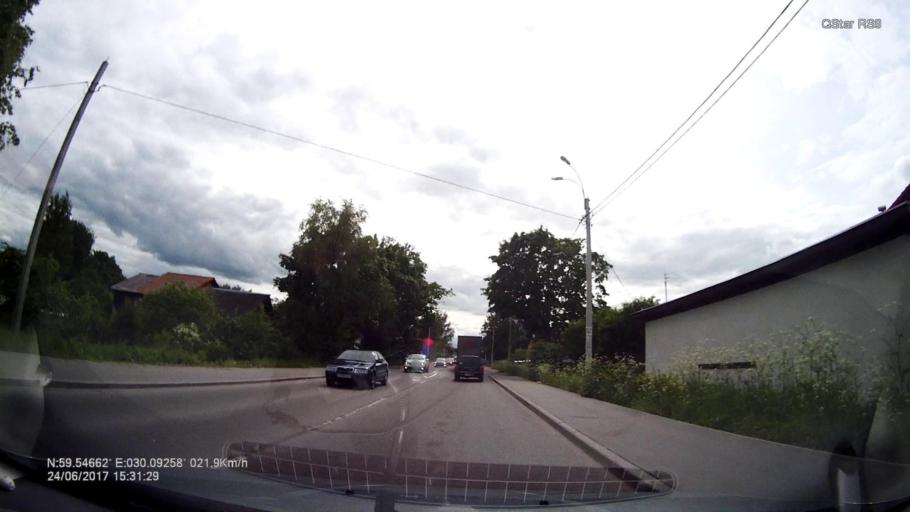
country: RU
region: Leningrad
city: Mariyenburg
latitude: 59.5465
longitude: 30.0925
